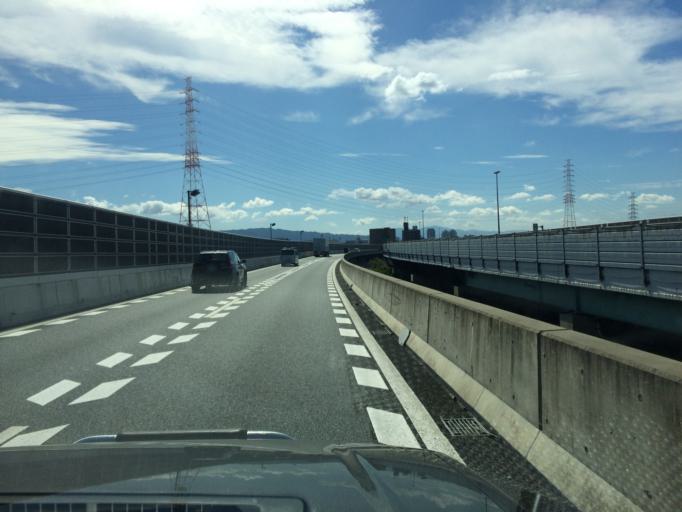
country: JP
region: Osaka
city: Daitocho
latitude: 34.7131
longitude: 135.5911
